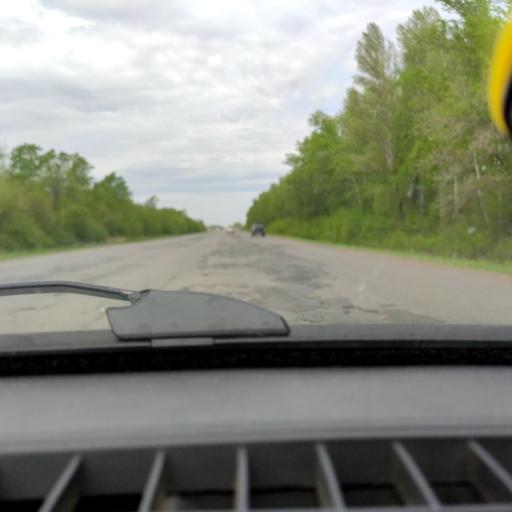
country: RU
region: Samara
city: Tol'yatti
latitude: 53.6519
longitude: 49.4234
